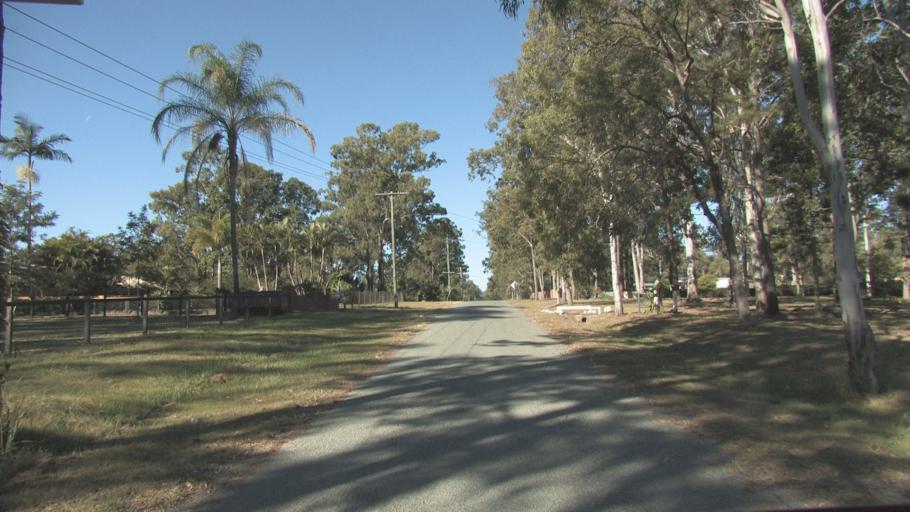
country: AU
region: Queensland
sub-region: Logan
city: Chambers Flat
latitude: -27.7601
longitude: 153.1164
